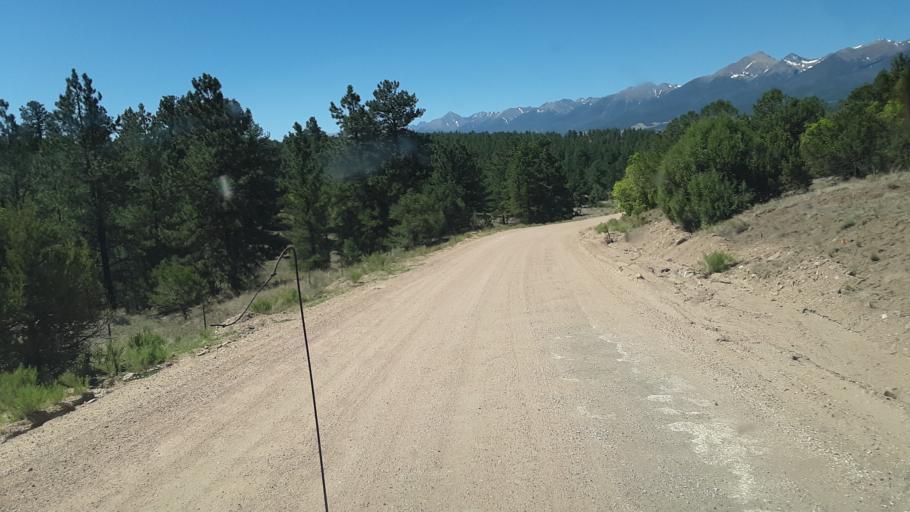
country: US
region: Colorado
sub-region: Custer County
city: Westcliffe
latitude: 38.2548
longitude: -105.5486
